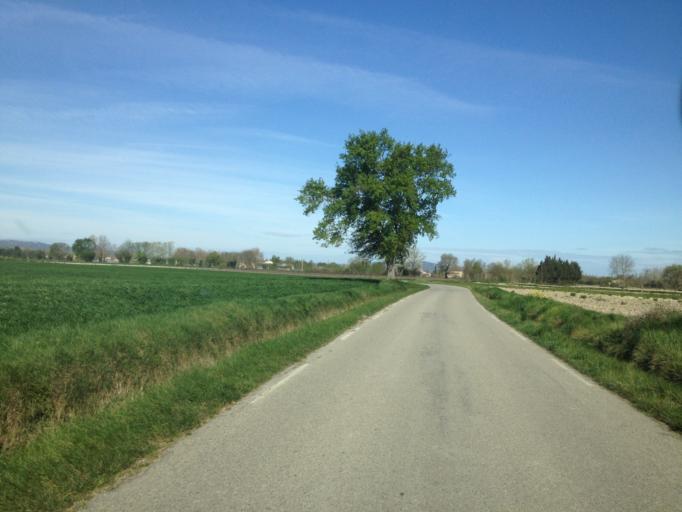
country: FR
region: Provence-Alpes-Cote d'Azur
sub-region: Departement du Vaucluse
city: Caderousse
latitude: 44.0960
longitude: 4.7720
